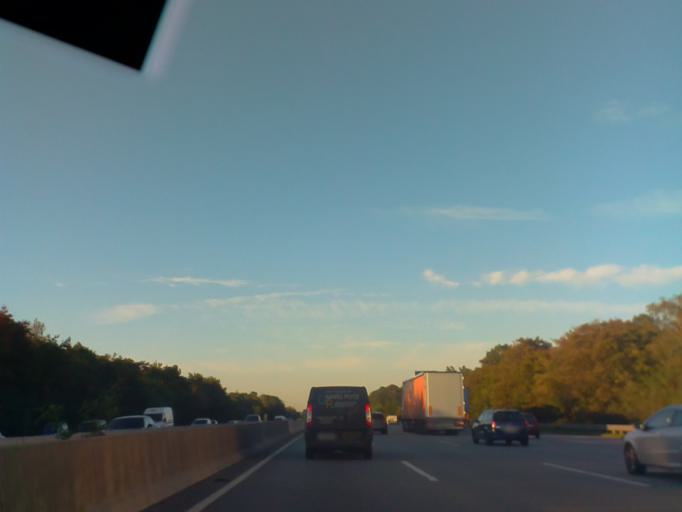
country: DE
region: Hesse
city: Weiterstadt
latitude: 49.9041
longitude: 8.6071
